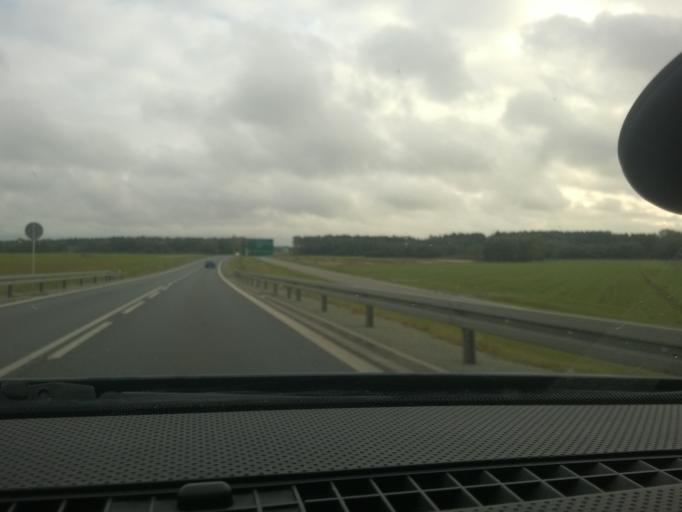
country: PL
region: Lodz Voivodeship
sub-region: Powiat sieradzki
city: Sieradz
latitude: 51.5590
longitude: 18.7156
